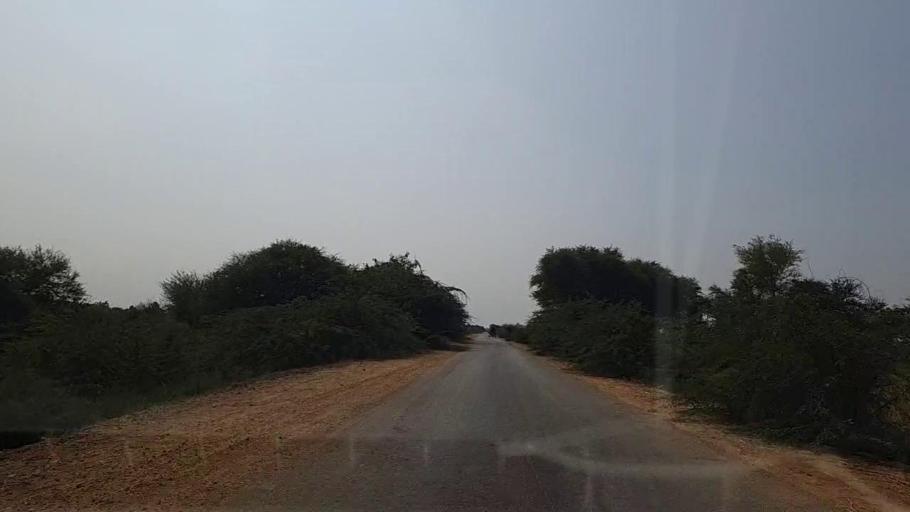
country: PK
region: Sindh
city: Chuhar Jamali
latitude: 24.2735
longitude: 67.9146
